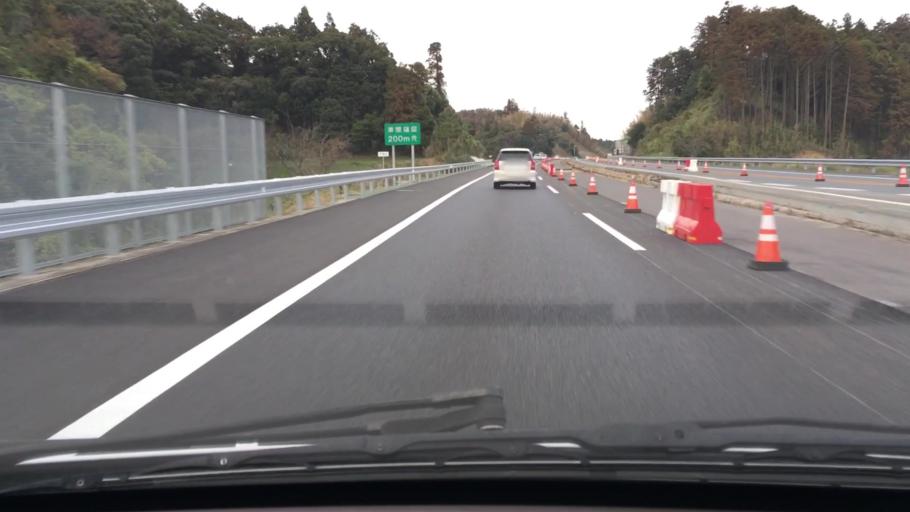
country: JP
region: Chiba
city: Kimitsu
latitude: 35.2871
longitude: 139.9282
